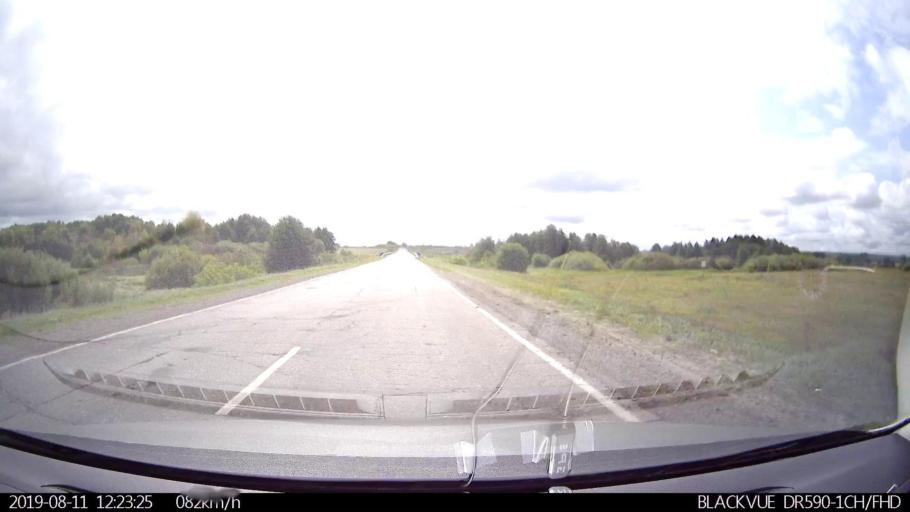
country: RU
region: Ulyanovsk
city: Ignatovka
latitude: 53.8956
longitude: 47.9505
